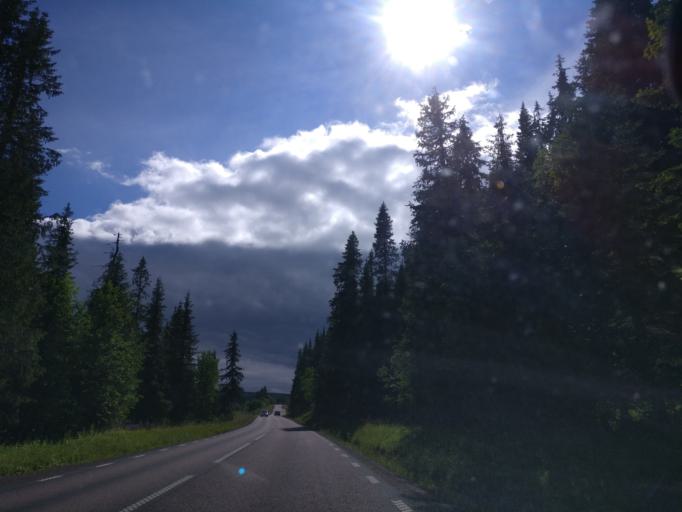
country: SE
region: Dalarna
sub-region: Malung-Saelens kommun
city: Malung
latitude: 61.1662
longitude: 13.1488
